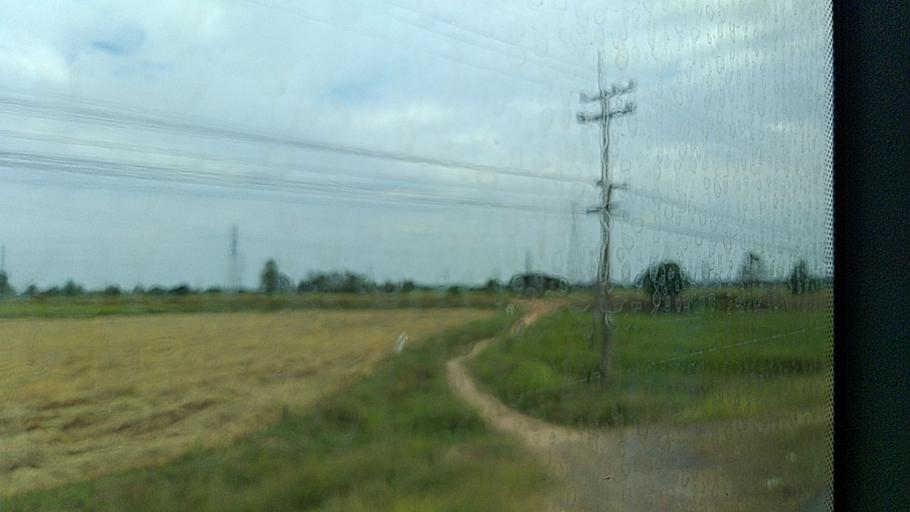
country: TH
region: Roi Et
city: Si Somdet
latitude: 16.1261
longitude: 103.4737
